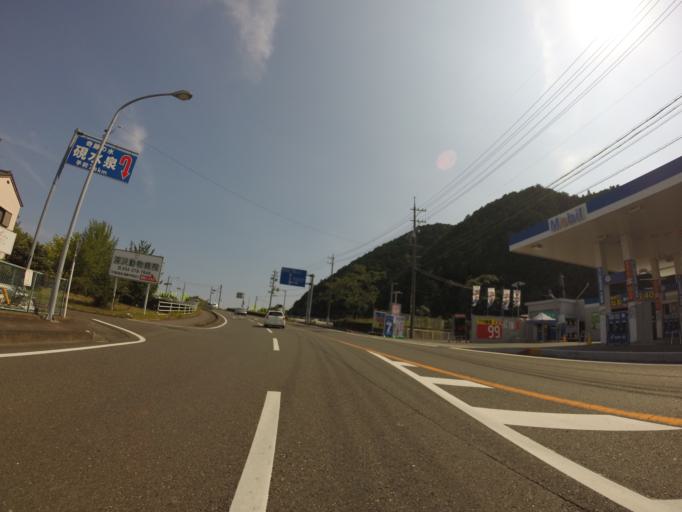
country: JP
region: Shizuoka
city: Shizuoka-shi
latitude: 35.0100
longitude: 138.3553
